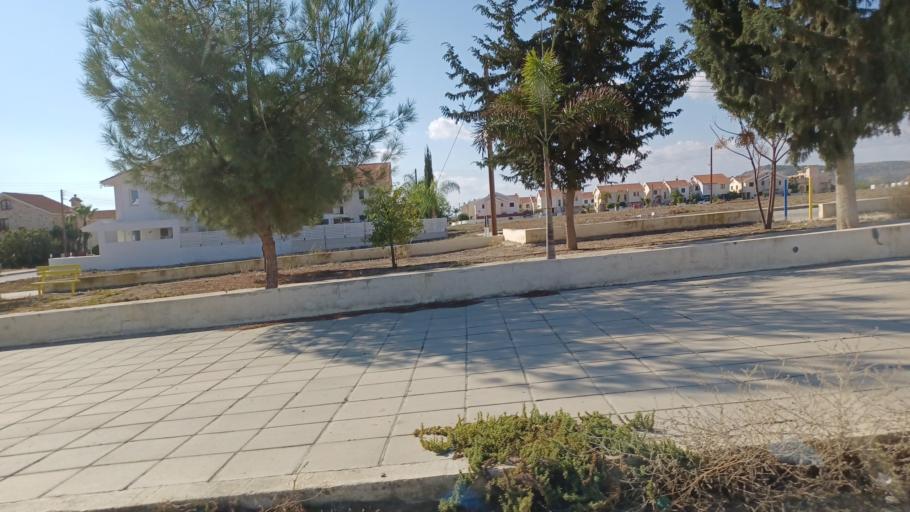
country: CY
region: Larnaka
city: Pyla
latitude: 34.9988
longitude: 33.6827
